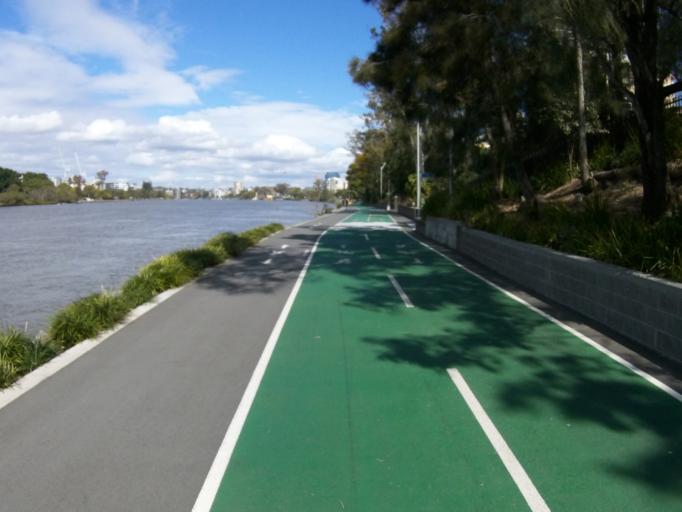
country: AU
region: Queensland
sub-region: Brisbane
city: Milton
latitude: -27.4756
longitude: 153.0030
